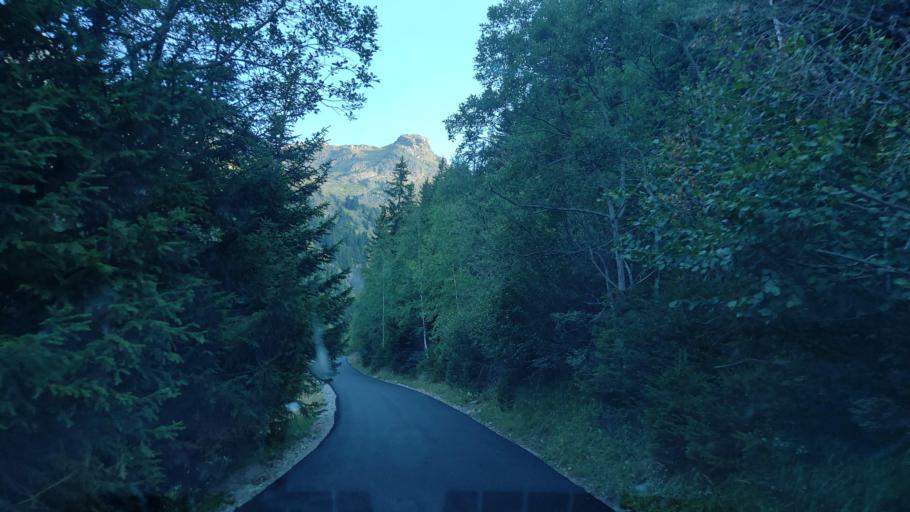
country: FR
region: Rhone-Alpes
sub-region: Departement de la Savoie
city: Val Thorens
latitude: 45.2248
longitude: 6.5548
